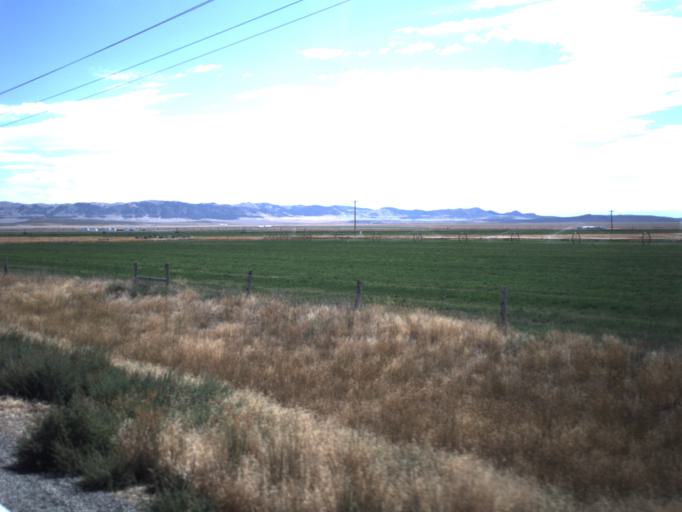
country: US
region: Idaho
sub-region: Oneida County
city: Malad City
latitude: 41.9667
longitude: -112.8850
